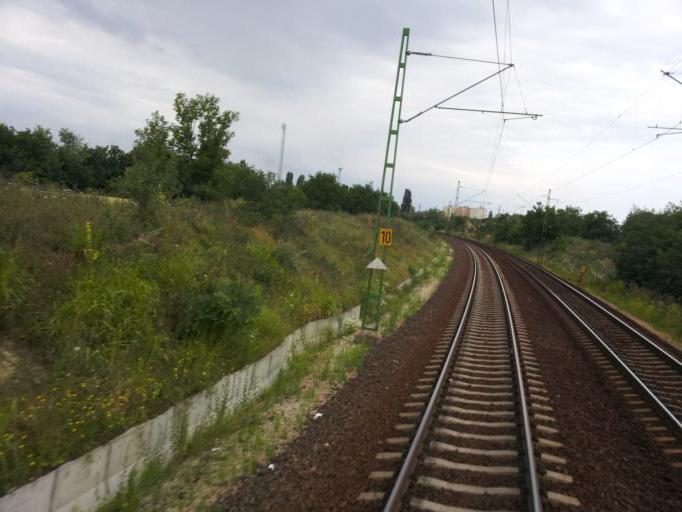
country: HU
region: Fejer
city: Szekesfehervar
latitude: 47.1859
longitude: 18.4396
